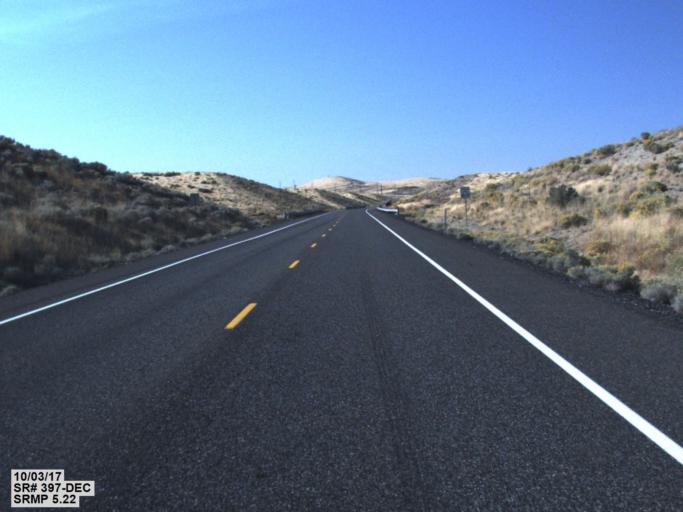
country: US
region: Washington
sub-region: Benton County
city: Highland
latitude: 46.1398
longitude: -119.1042
